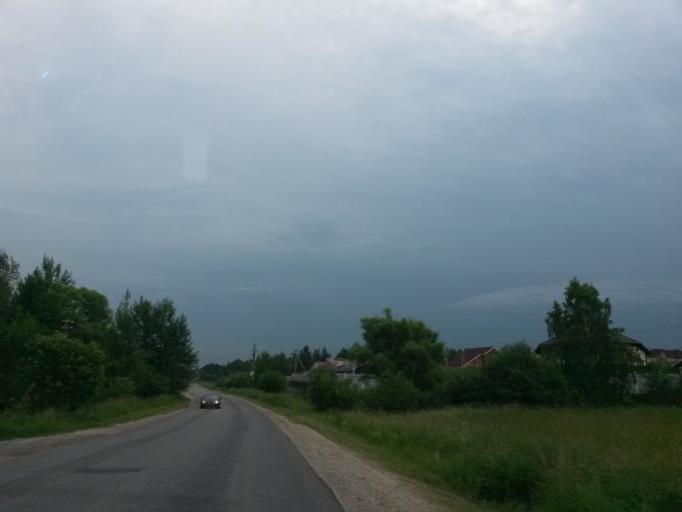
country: RU
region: Moskovskaya
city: Lyubuchany
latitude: 55.2654
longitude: 37.6137
